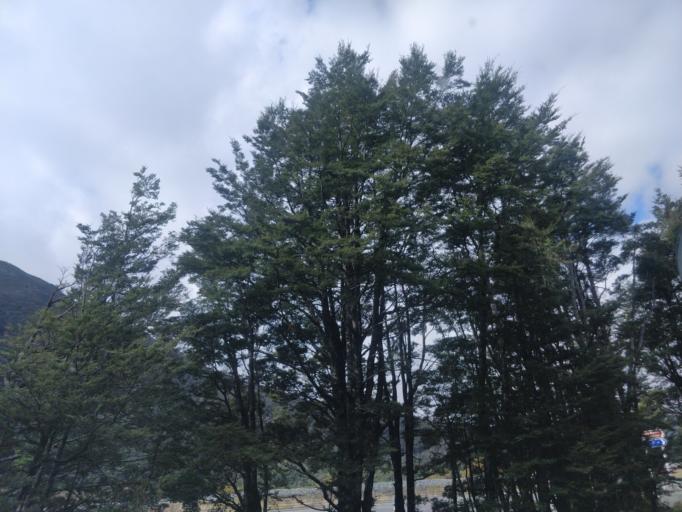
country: NZ
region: West Coast
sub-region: Grey District
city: Greymouth
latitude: -42.9841
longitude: 171.5906
